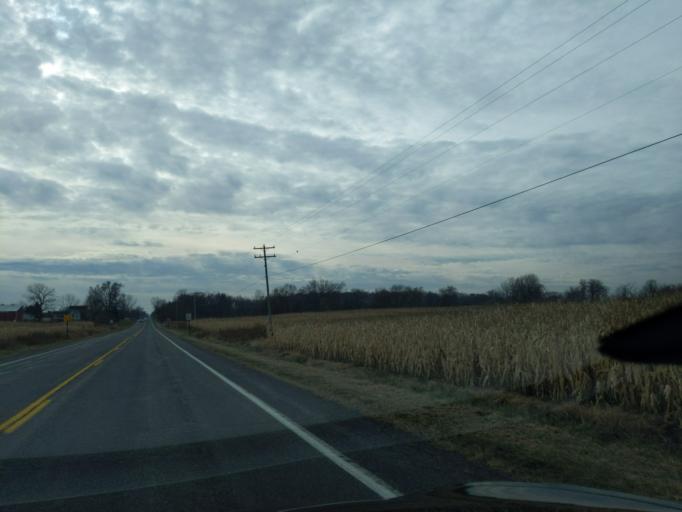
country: US
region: Michigan
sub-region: Ingham County
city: Holt
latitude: 42.5948
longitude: -84.5230
